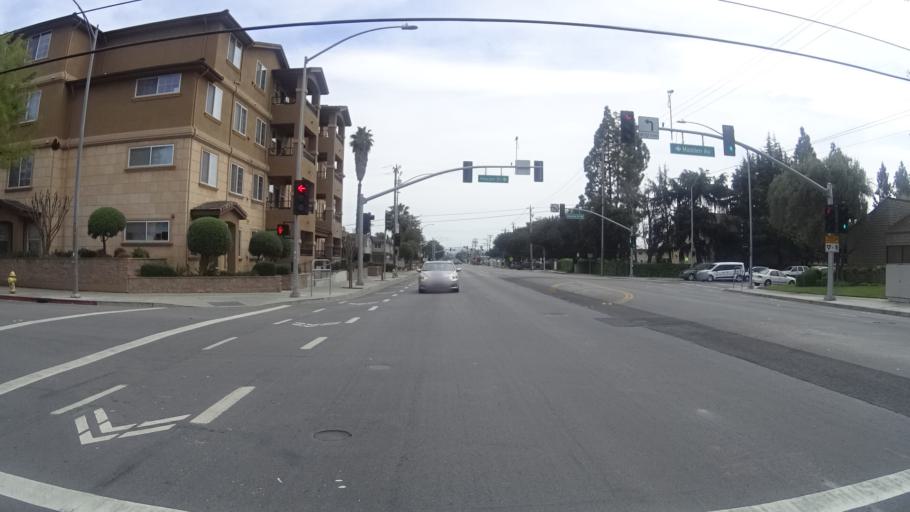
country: US
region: California
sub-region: Santa Clara County
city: Alum Rock
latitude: 37.3613
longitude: -121.8461
